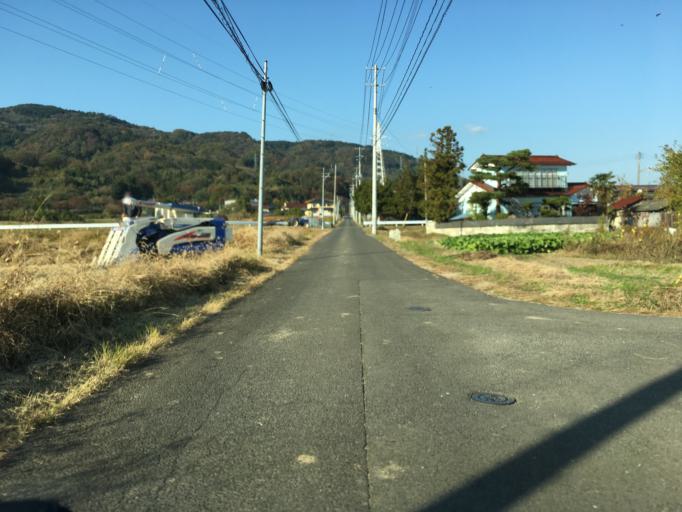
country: JP
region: Fukushima
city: Hobaramachi
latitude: 37.8311
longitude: 140.4943
